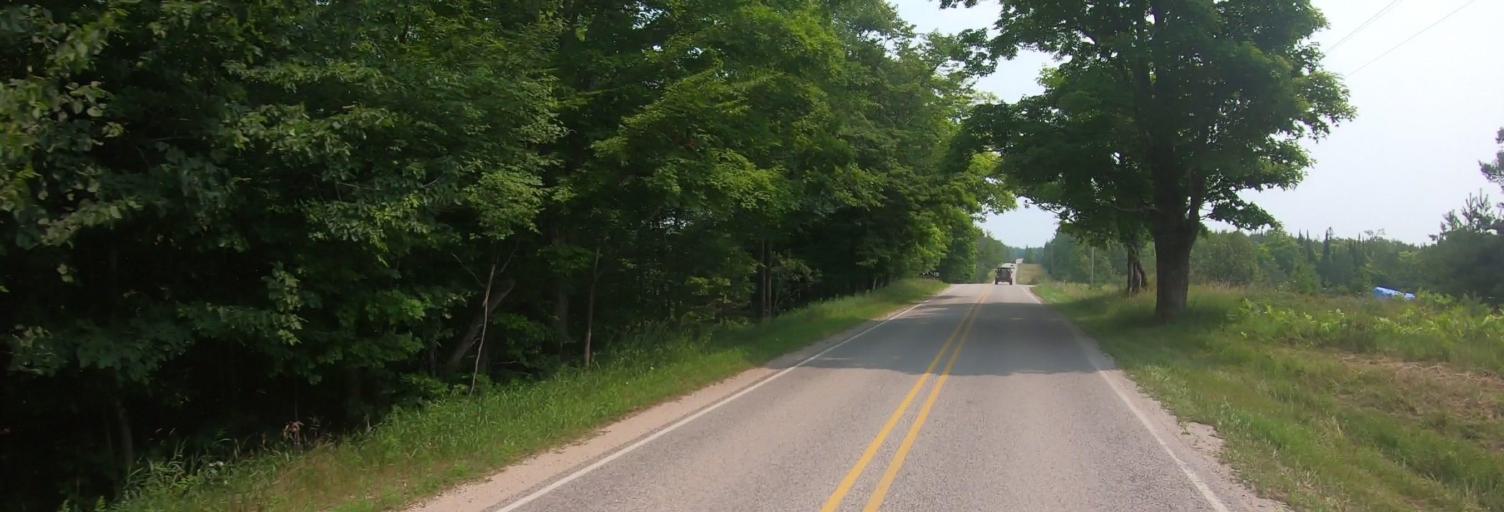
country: CA
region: Ontario
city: Thessalon
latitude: 45.9987
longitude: -83.7228
